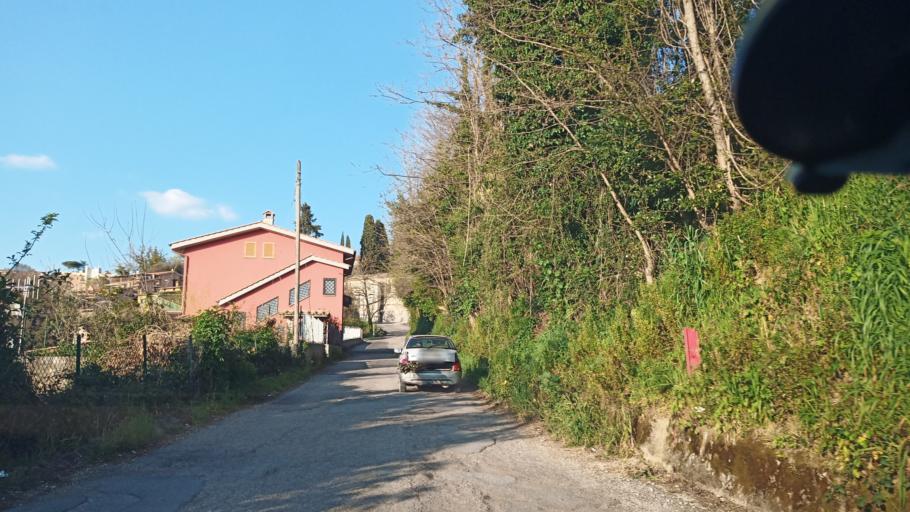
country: IT
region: Latium
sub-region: Provincia di Rieti
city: Poggio Mirteto
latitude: 42.2670
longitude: 12.6843
